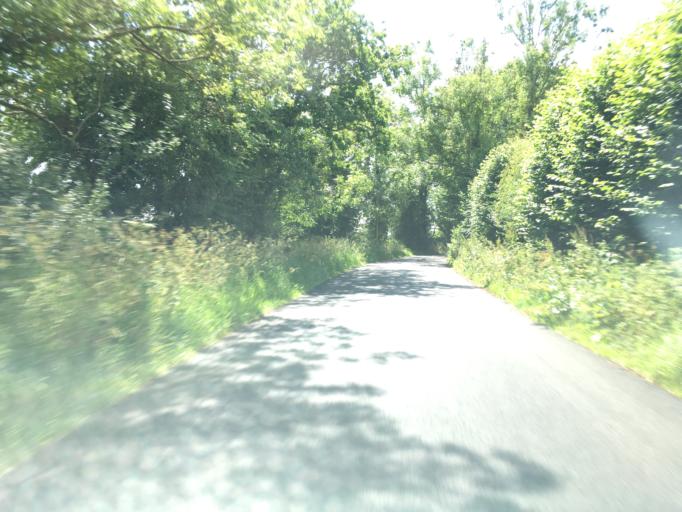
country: GB
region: England
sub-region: Gloucestershire
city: Tetbury
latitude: 51.6324
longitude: -2.1887
